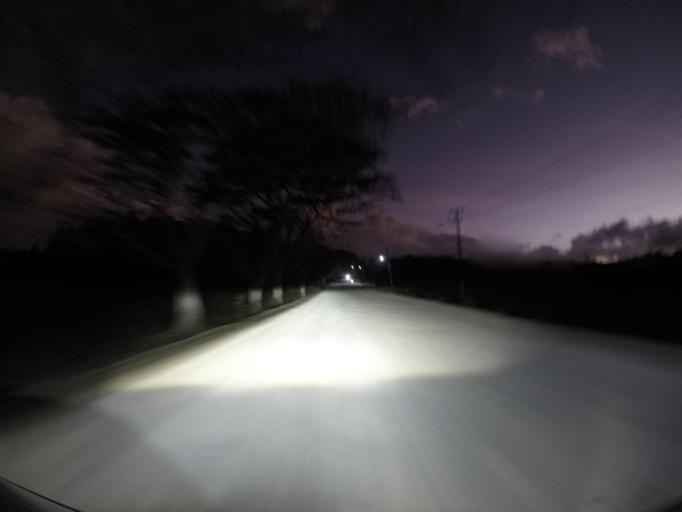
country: TL
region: Lautem
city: Lospalos
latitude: -8.4522
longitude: 127.0009
